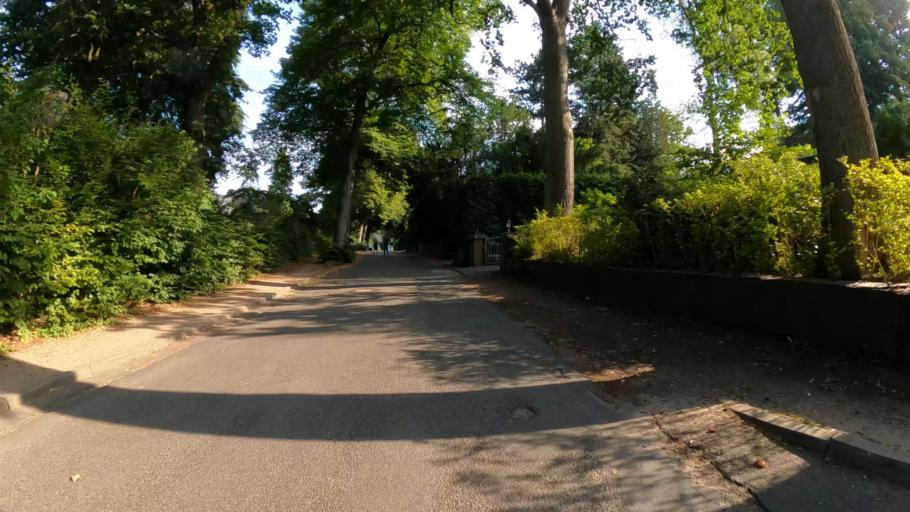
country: DE
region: Schleswig-Holstein
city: Wentorf bei Hamburg
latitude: 53.4989
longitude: 10.2428
